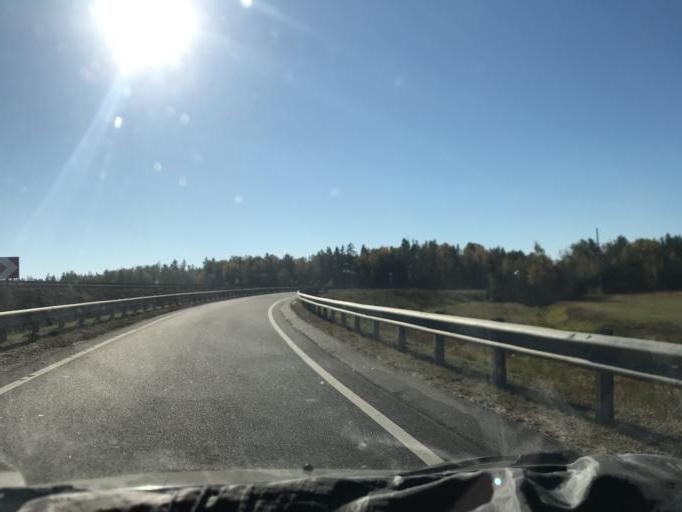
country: BY
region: Mogilev
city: Babruysk
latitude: 53.2079
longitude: 29.0719
